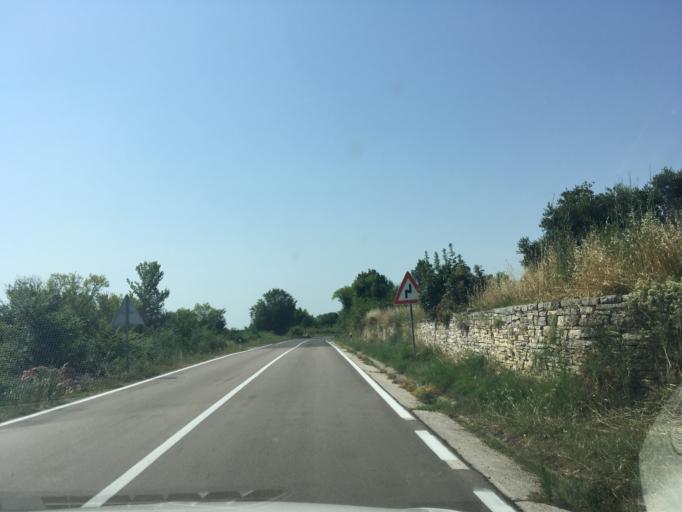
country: HR
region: Zadarska
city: Benkovac
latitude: 44.0158
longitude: 15.6452
